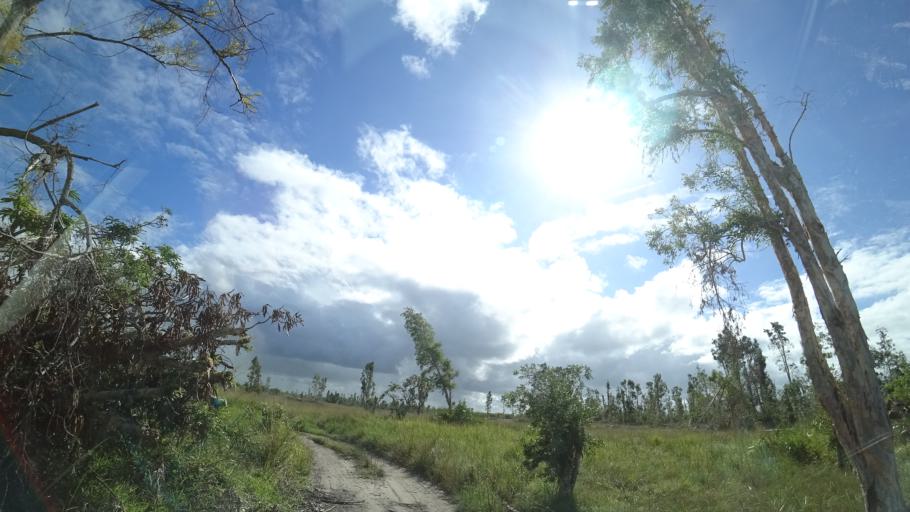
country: MZ
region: Sofala
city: Beira
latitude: -19.5751
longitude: 35.2564
